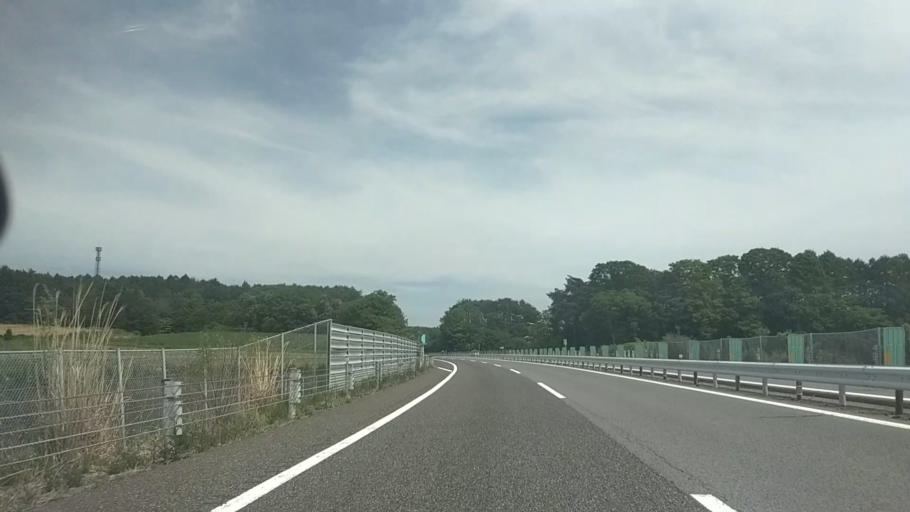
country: JP
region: Nagano
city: Chino
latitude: 35.9064
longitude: 138.2585
